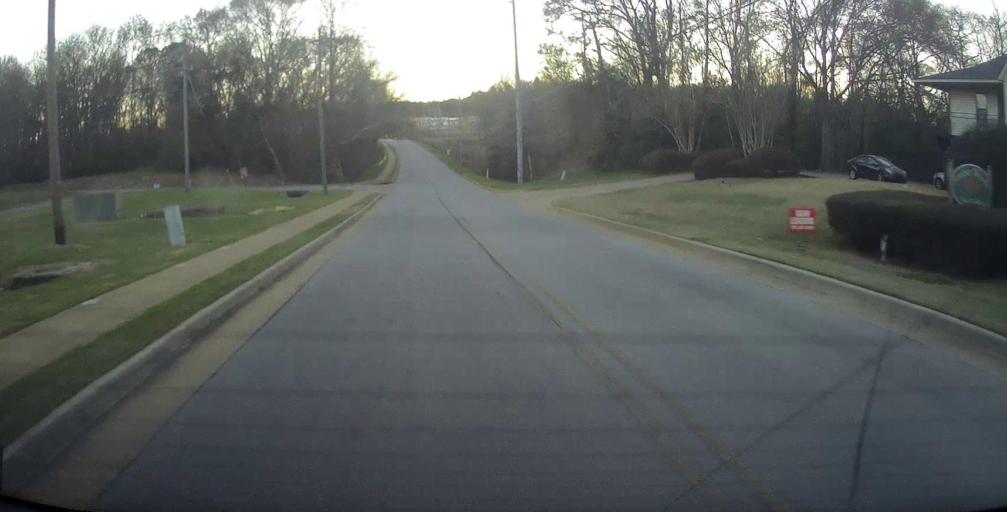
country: US
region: Alabama
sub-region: Russell County
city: Phenix City
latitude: 32.4844
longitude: -85.0273
